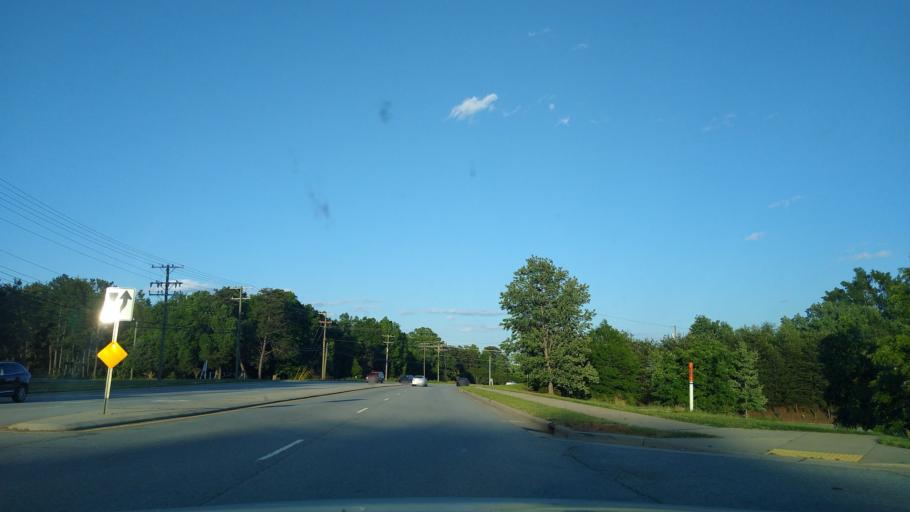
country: US
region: North Carolina
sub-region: Guilford County
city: Oak Ridge
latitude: 36.1044
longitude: -79.9866
